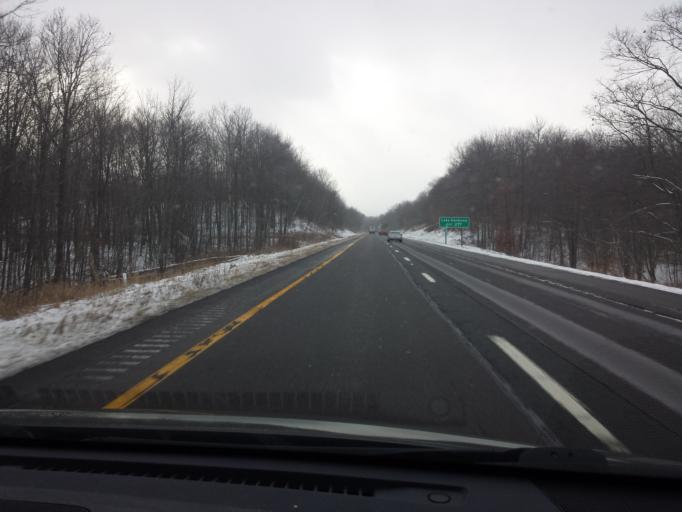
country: US
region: Pennsylvania
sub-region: Luzerne County
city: White Haven
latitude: 41.0769
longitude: -75.6722
